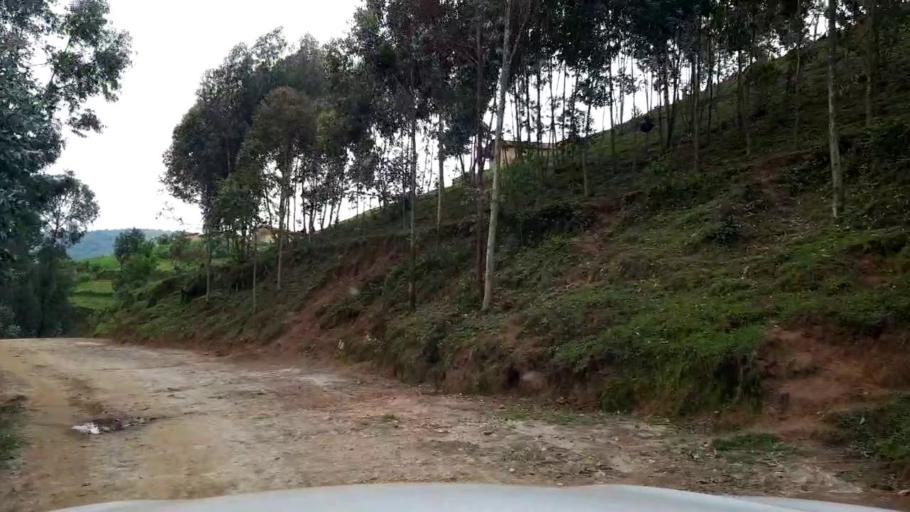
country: RW
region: Western Province
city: Kibuye
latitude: -1.9628
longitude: 29.4779
